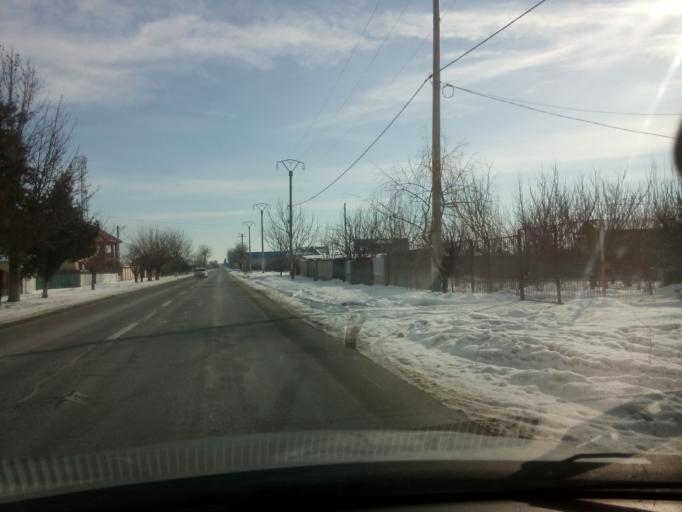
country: RO
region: Calarasi
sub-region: Comuna Frumusani
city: Frumusani
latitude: 44.3067
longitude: 26.2965
